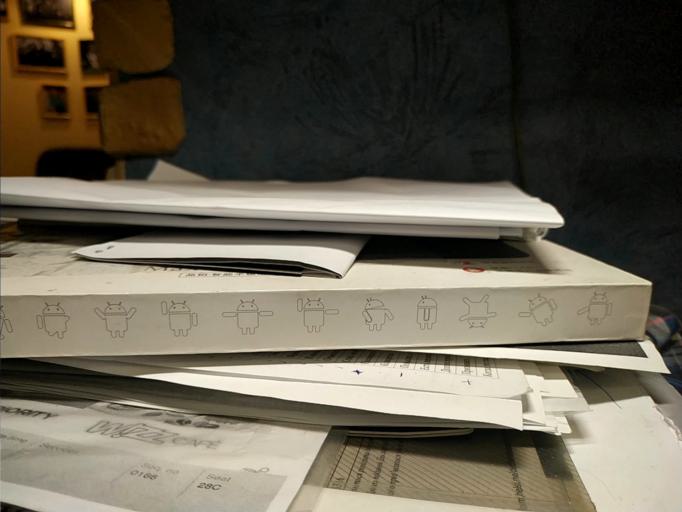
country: RU
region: Tverskaya
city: Zubtsov
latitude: 56.0835
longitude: 34.7834
